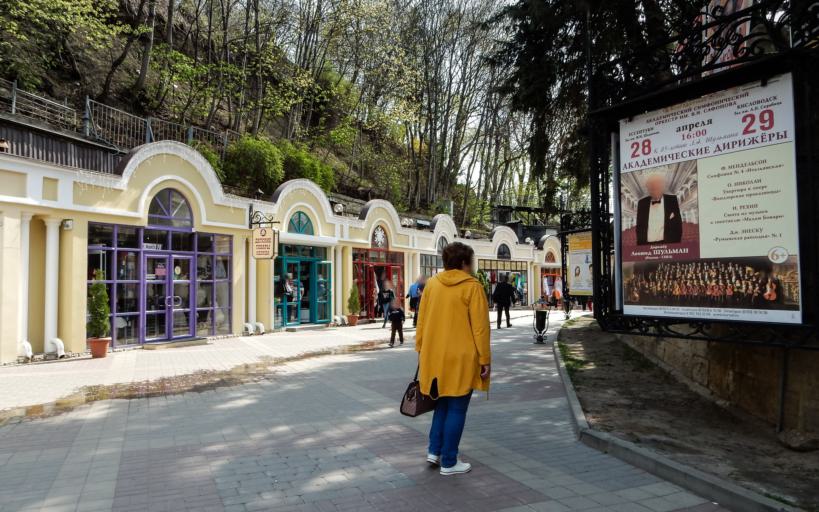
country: RU
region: Stavropol'skiy
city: Kislovodsk
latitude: 43.9012
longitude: 42.7200
